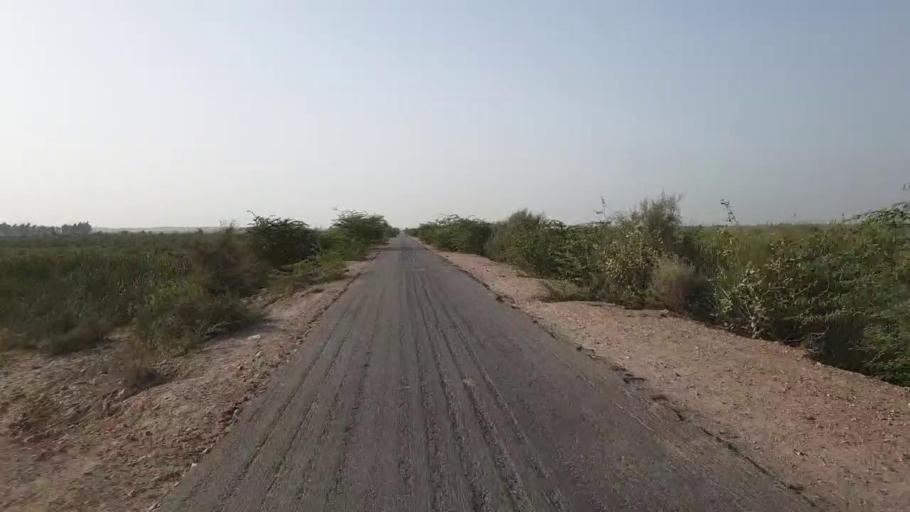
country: PK
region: Sindh
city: Jam Sahib
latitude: 26.4404
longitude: 68.8666
